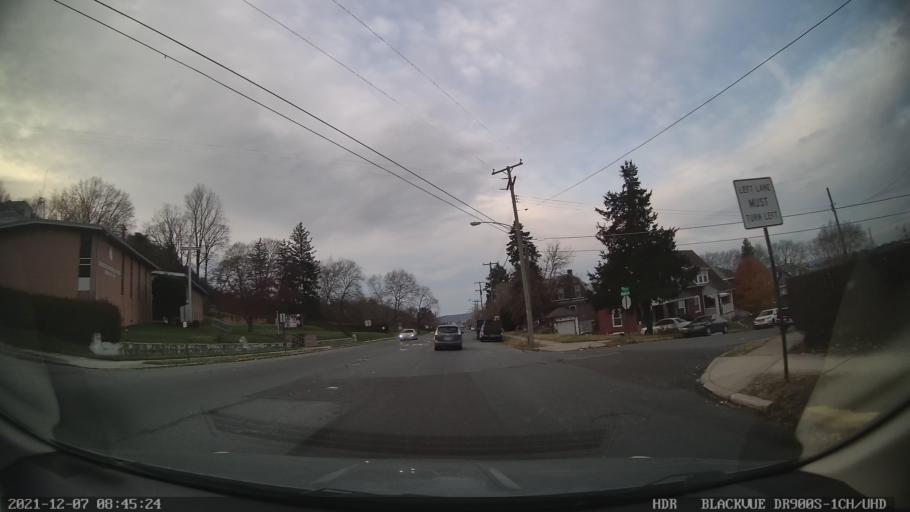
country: US
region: Pennsylvania
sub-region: Berks County
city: Reading
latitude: 40.3548
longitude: -75.9090
